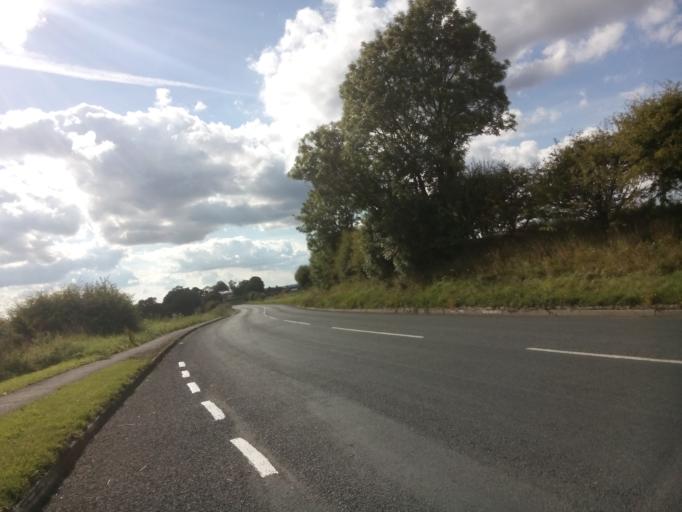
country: GB
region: England
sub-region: County Durham
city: Pittington
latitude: 54.7868
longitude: -1.4982
